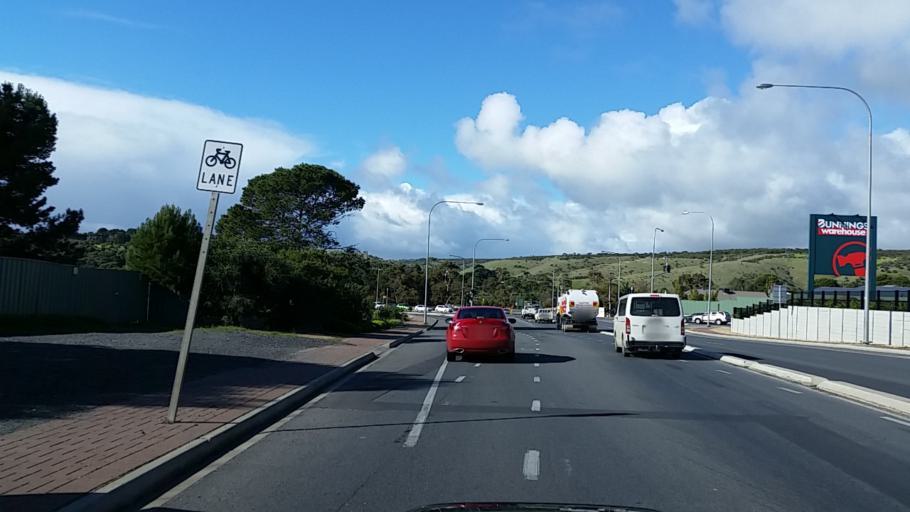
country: AU
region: South Australia
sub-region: Onkaparinga
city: Noarlunga
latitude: -35.1801
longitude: 138.4945
